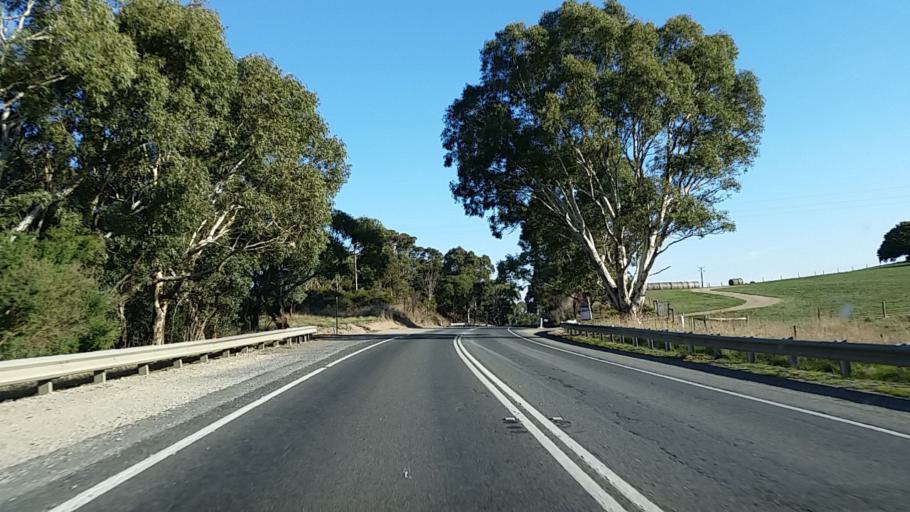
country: AU
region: South Australia
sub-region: Mount Barker
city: Macclesfield
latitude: -35.1420
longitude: 138.8867
